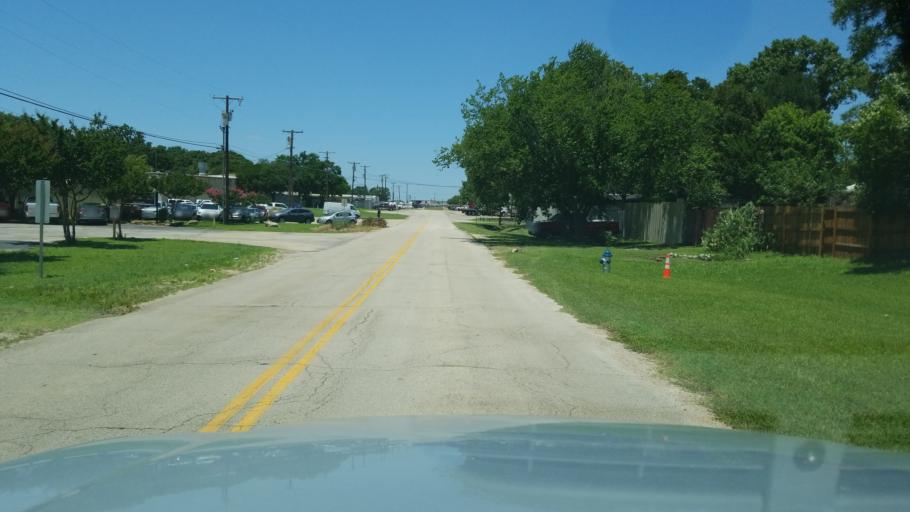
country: US
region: Texas
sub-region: Dallas County
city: Irving
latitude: 32.8042
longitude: -96.9178
